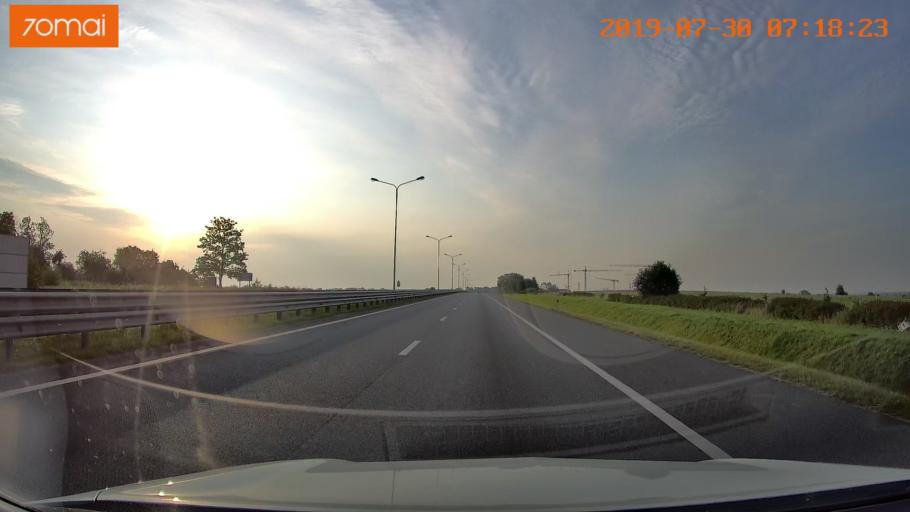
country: RU
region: Kaliningrad
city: Bol'shoe Isakovo
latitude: 54.7042
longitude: 20.6473
